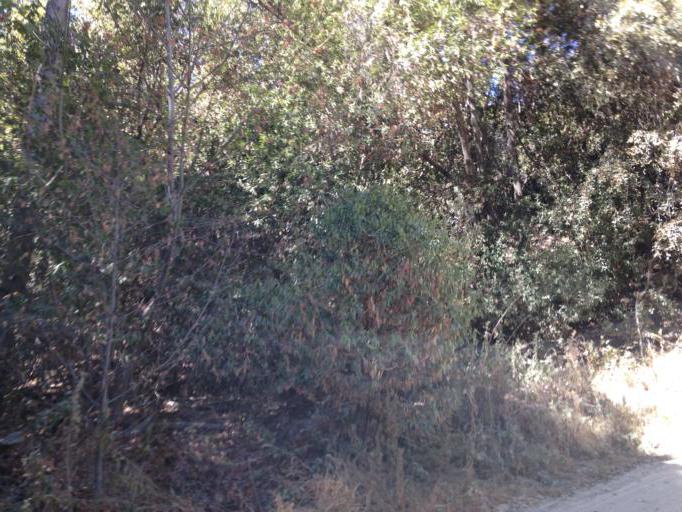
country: US
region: California
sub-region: San Bernardino County
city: Running Springs
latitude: 34.1675
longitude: -117.0772
